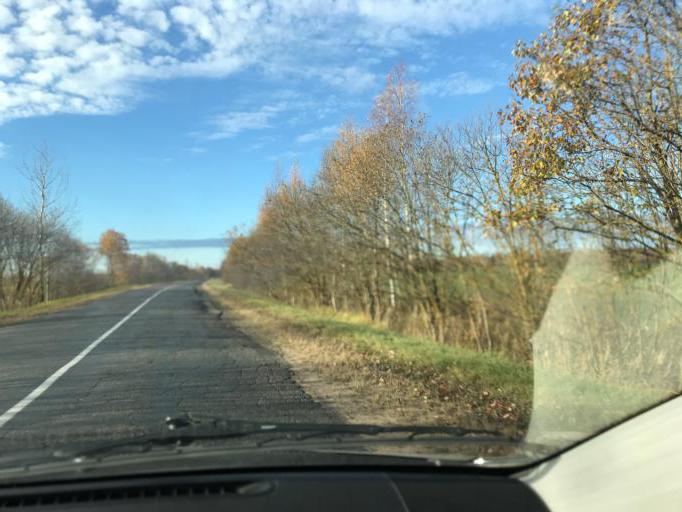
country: BY
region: Vitebsk
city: Haradok
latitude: 55.4049
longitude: 29.7341
